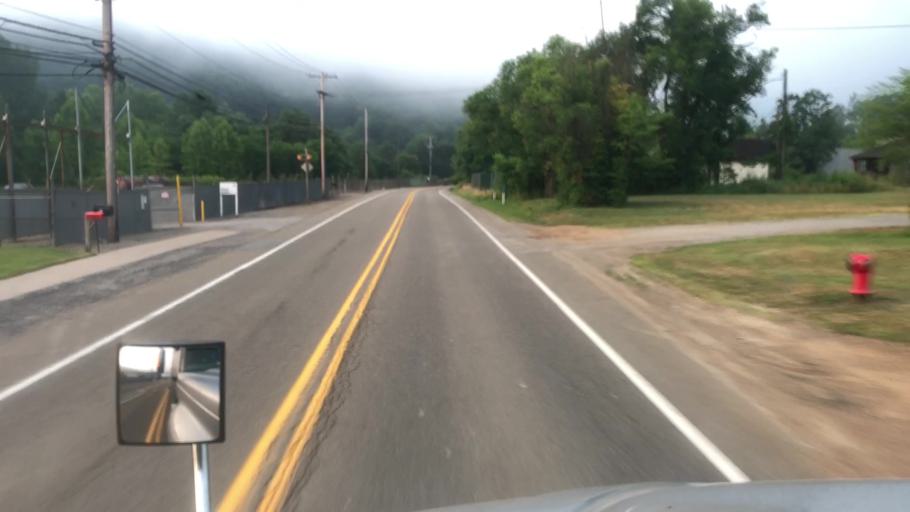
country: US
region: Pennsylvania
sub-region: Venango County
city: Hasson Heights
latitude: 41.4524
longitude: -79.6897
